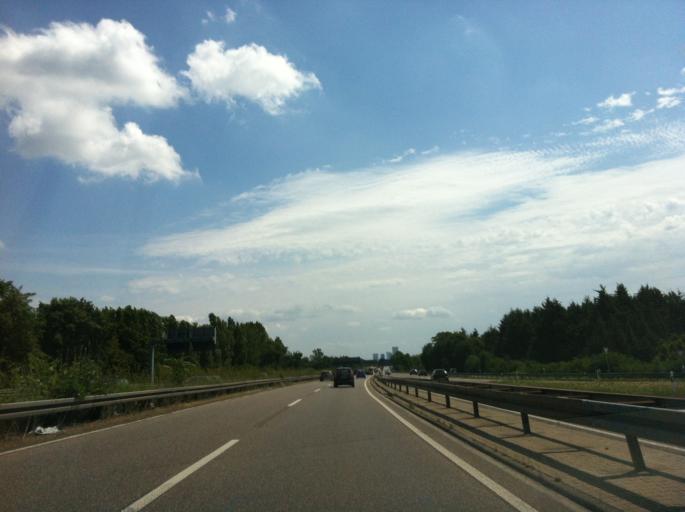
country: DE
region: Hesse
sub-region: Regierungsbezirk Darmstadt
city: Eschborn
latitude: 50.1345
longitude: 8.5932
